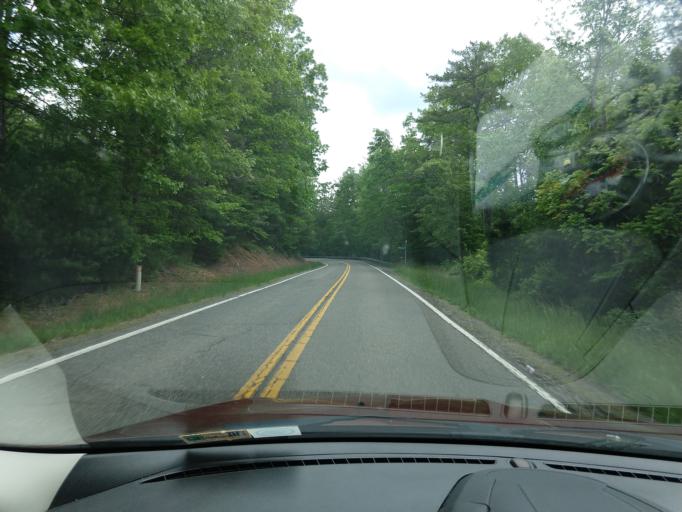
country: US
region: Virginia
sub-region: City of Galax
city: Galax
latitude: 36.7981
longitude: -80.9897
